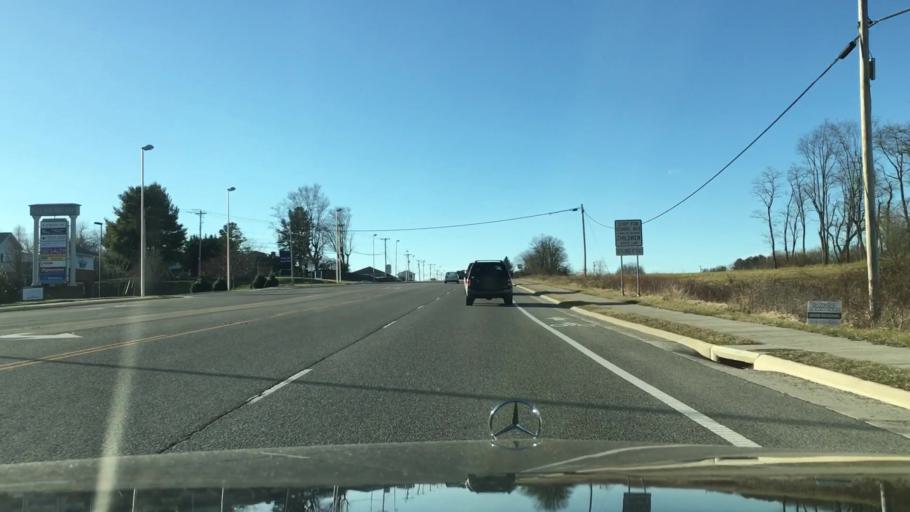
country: US
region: Virginia
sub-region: Montgomery County
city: Merrimac
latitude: 37.1623
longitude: -80.4318
